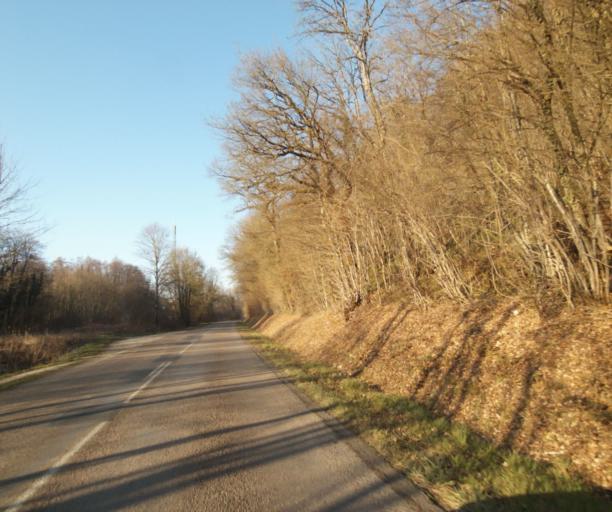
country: FR
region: Champagne-Ardenne
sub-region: Departement de la Haute-Marne
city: Chevillon
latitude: 48.5288
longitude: 5.1089
